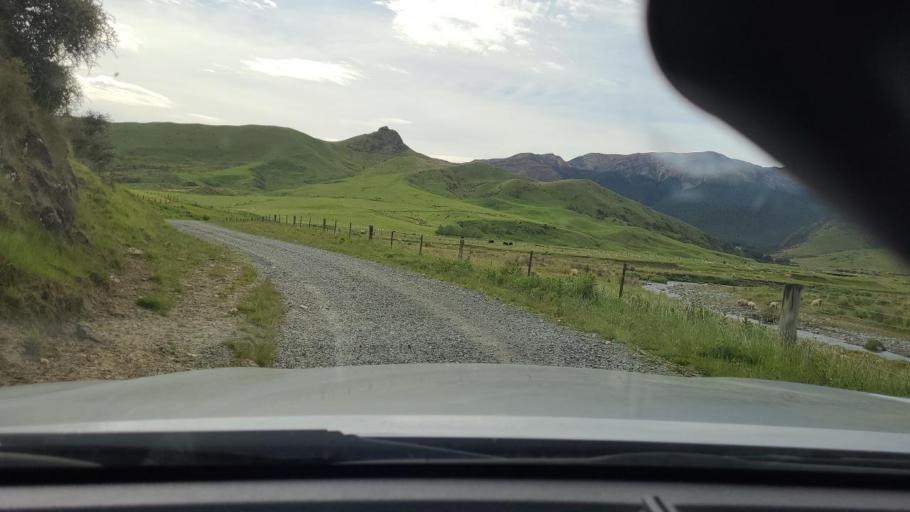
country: NZ
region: Southland
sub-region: Southland District
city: Te Anau
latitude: -45.5660
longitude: 167.9466
